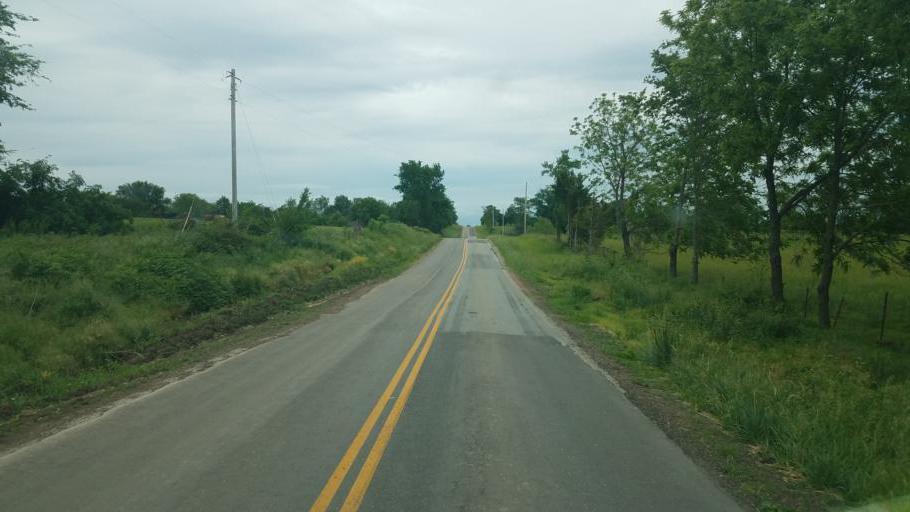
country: US
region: Missouri
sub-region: Moniteau County
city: California
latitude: 38.6990
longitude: -92.6350
